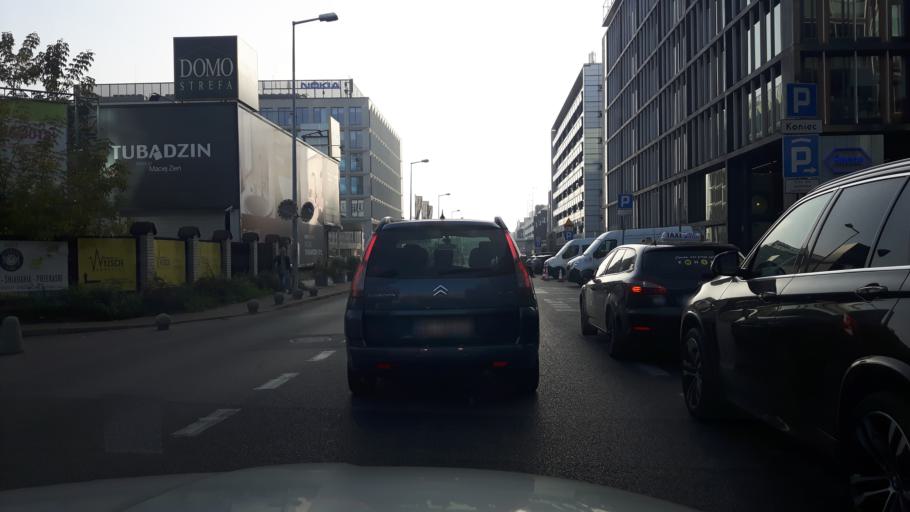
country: PL
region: Masovian Voivodeship
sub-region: Warszawa
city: Mokotow
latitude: 52.1824
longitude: 21.0059
